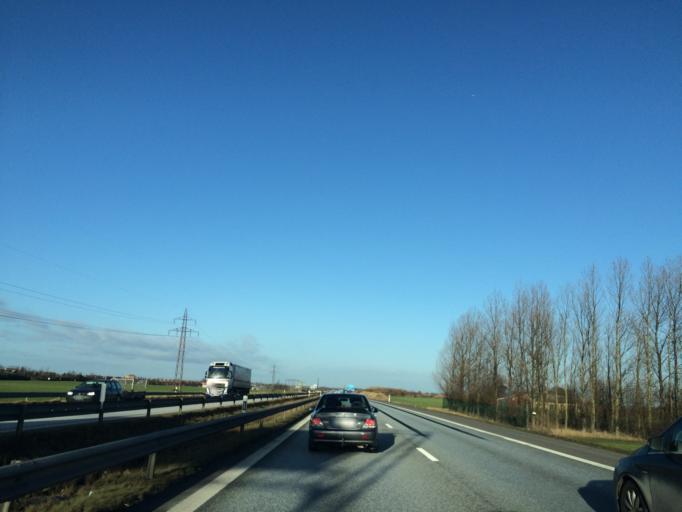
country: SE
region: Skane
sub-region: Lomma Kommun
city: Lomma
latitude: 55.6689
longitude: 13.0997
